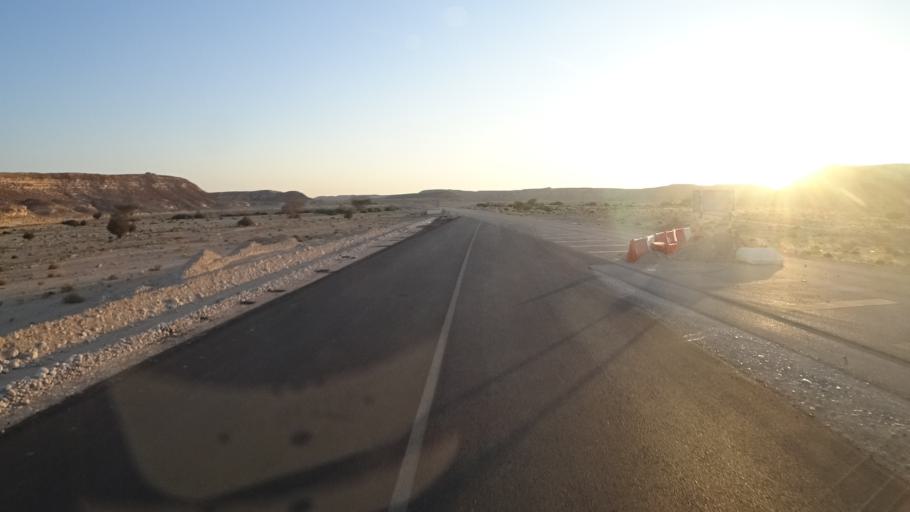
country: OM
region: Zufar
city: Salalah
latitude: 17.5141
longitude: 53.3726
